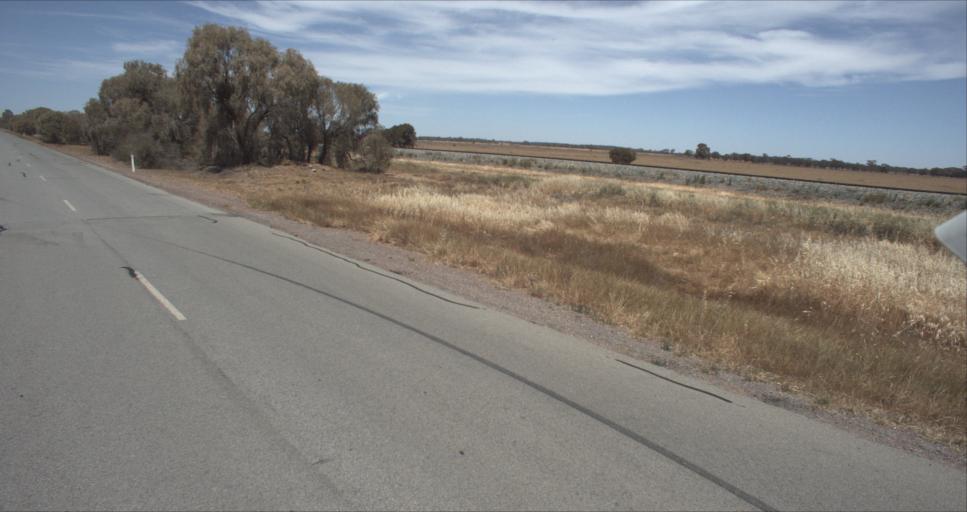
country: AU
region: New South Wales
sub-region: Leeton
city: Leeton
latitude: -34.6298
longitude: 146.4552
